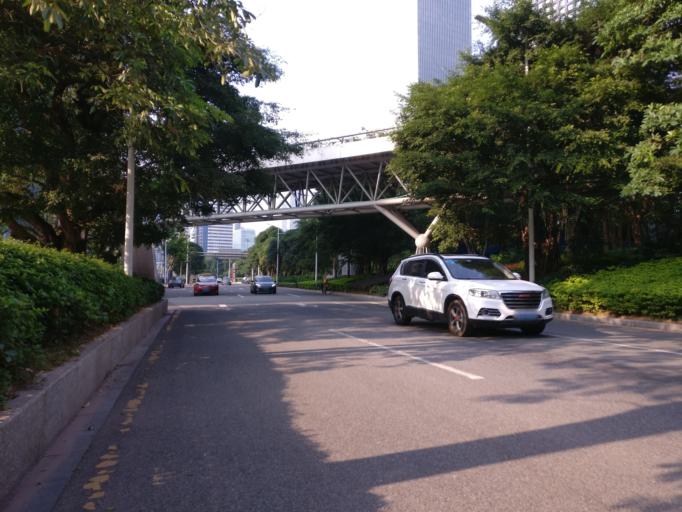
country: CN
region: Guangdong
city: Wushan
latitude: 23.1262
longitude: 113.3179
